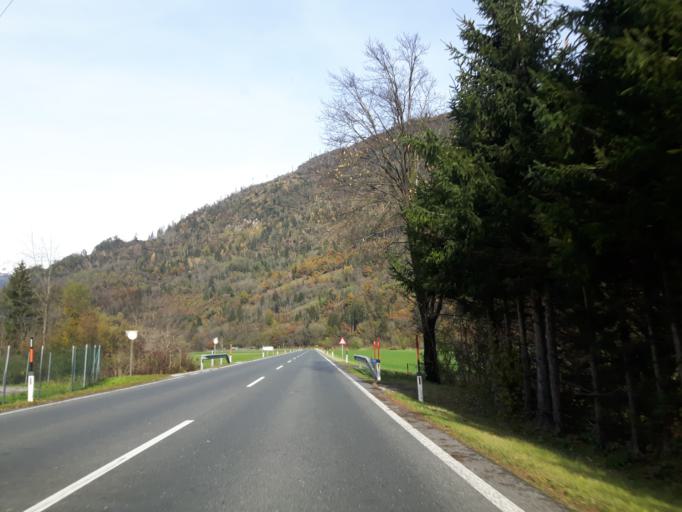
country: AT
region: Tyrol
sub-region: Politischer Bezirk Lienz
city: Lavant
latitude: 46.7964
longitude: 12.8744
